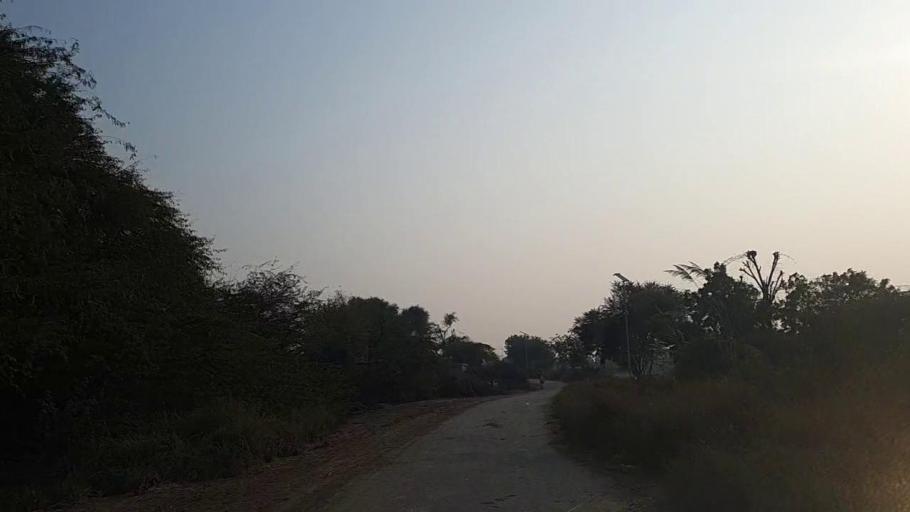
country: PK
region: Sindh
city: Nawabshah
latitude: 26.2125
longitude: 68.4720
